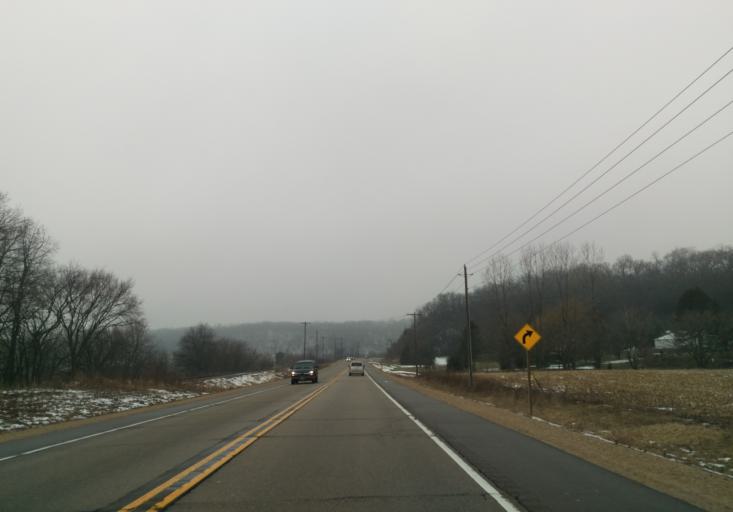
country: US
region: Wisconsin
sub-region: Dane County
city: Cross Plains
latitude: 43.0920
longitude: -89.5846
